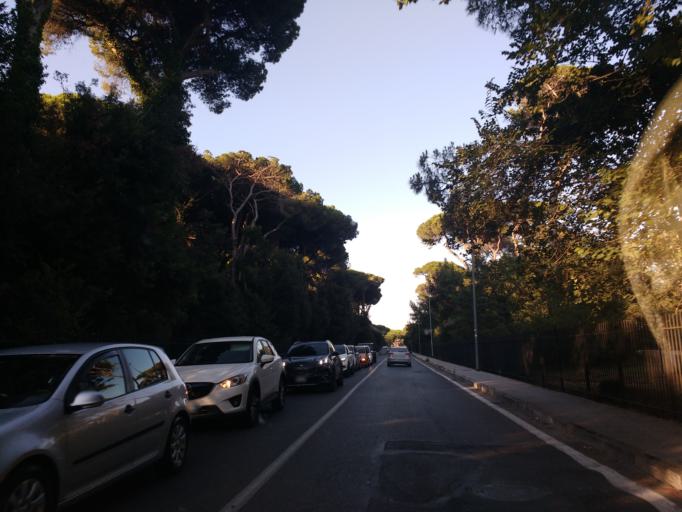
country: IT
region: Latium
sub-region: Citta metropolitana di Roma Capitale
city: Fregene
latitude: 41.8562
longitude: 12.1988
